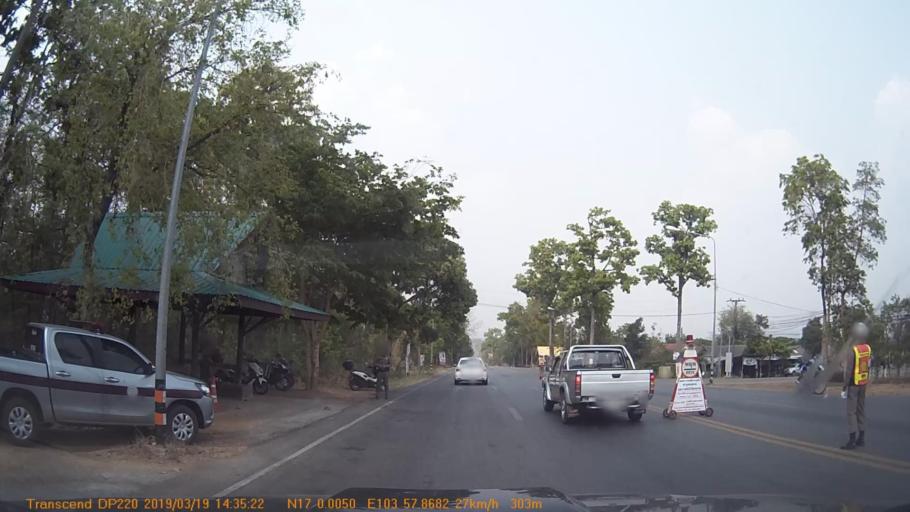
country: TH
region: Sakon Nakhon
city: Phu Phan
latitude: 17.0003
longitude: 103.9646
